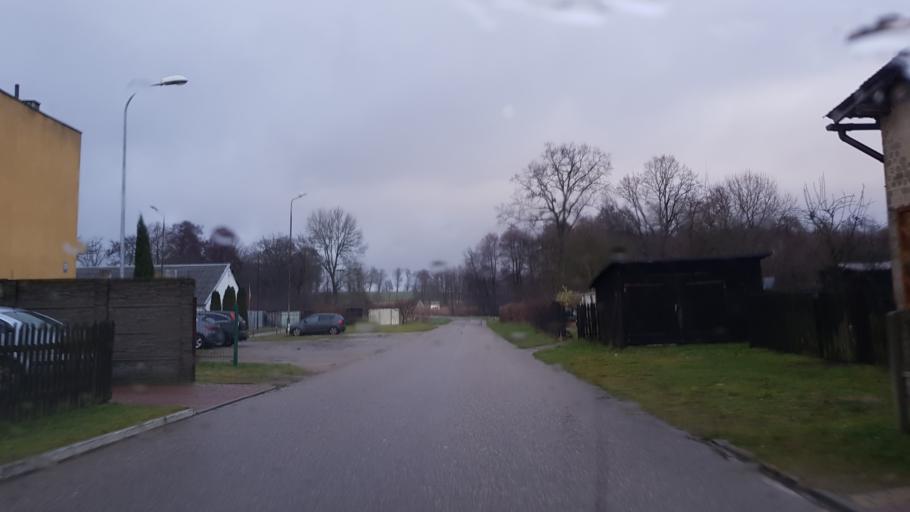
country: PL
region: West Pomeranian Voivodeship
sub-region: Powiat bialogardzki
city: Bialogard
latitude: 53.9365
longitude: 16.0048
